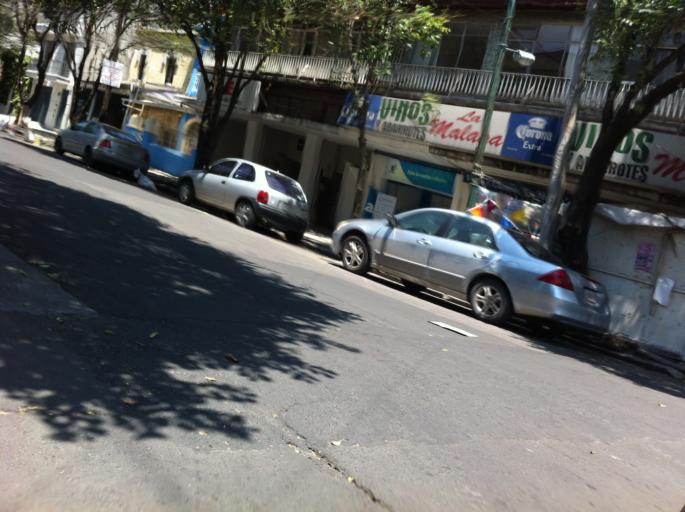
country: MX
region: Mexico City
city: Benito Juarez
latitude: 19.4164
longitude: -99.1570
